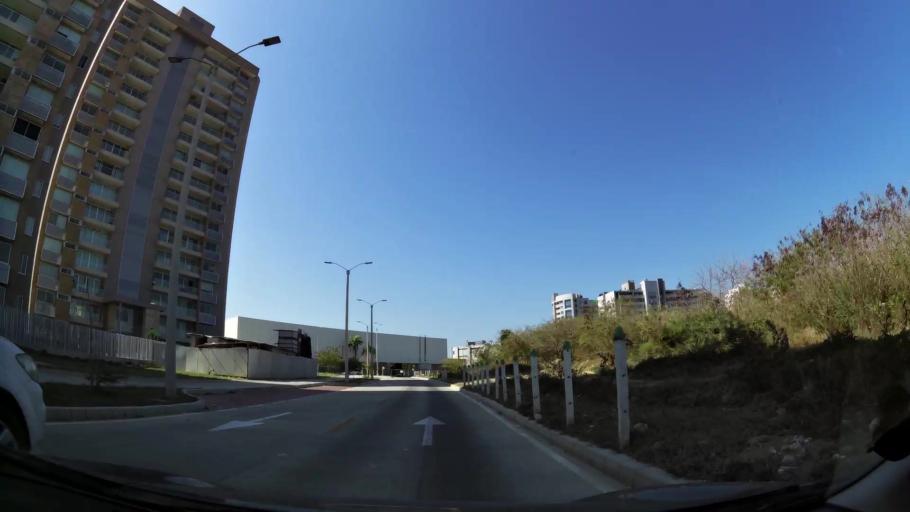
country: CO
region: Atlantico
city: Barranquilla
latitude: 11.0173
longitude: -74.8289
